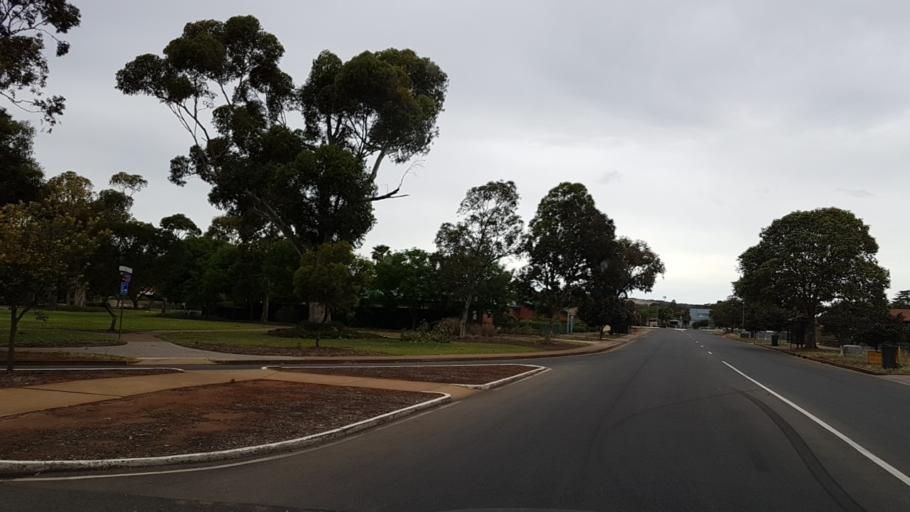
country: AU
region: South Australia
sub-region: Salisbury
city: Elizabeth
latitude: -34.7352
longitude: 138.6702
